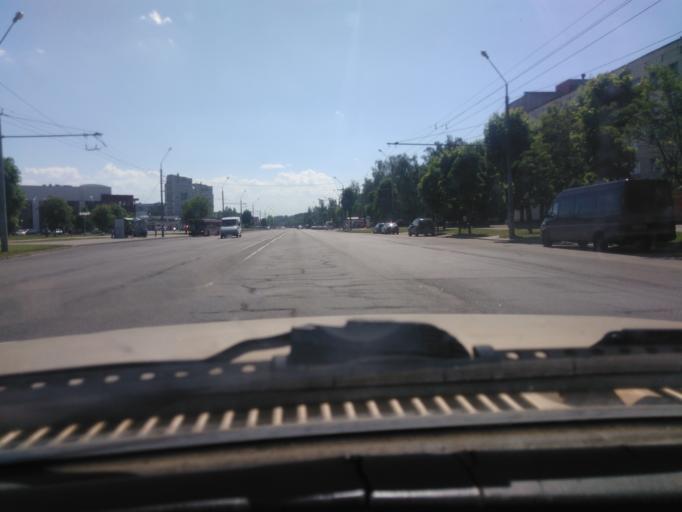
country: BY
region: Mogilev
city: Palykavichy Pyershyya
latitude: 53.9529
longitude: 30.3617
